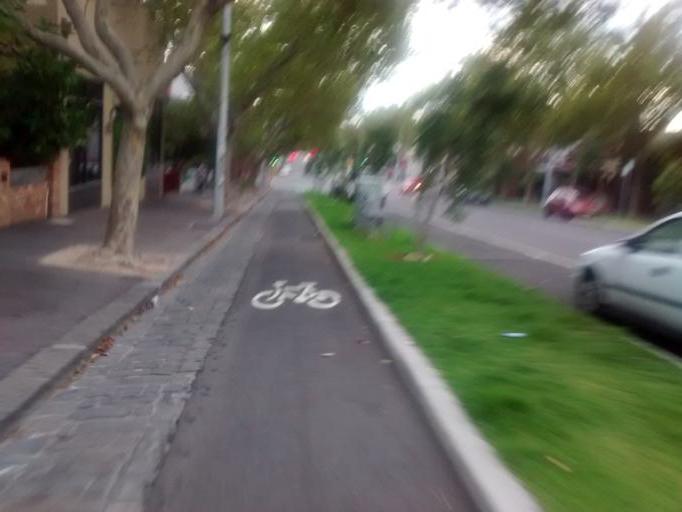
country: AU
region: Victoria
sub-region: Melbourne
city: North Melbourne
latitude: -37.8035
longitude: 144.9453
